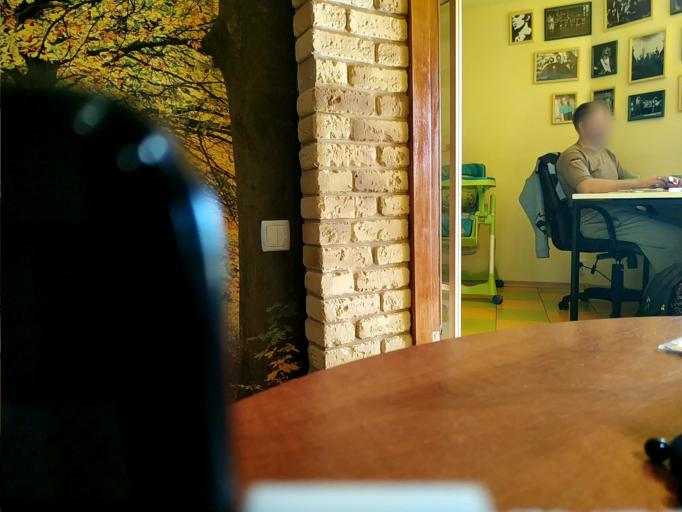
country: RU
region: Tverskaya
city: Vasil'yevskiy Mokh
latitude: 57.1359
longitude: 35.8520
